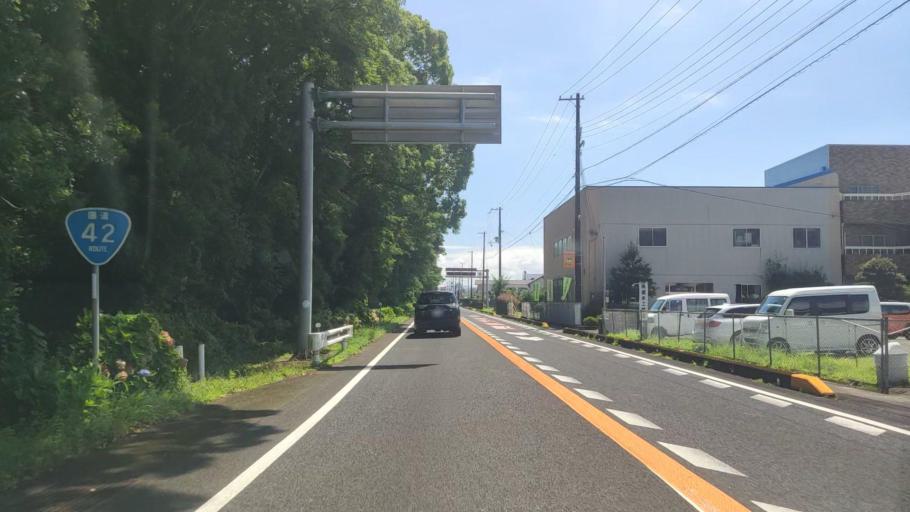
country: JP
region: Wakayama
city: Shingu
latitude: 33.8694
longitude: 136.0834
